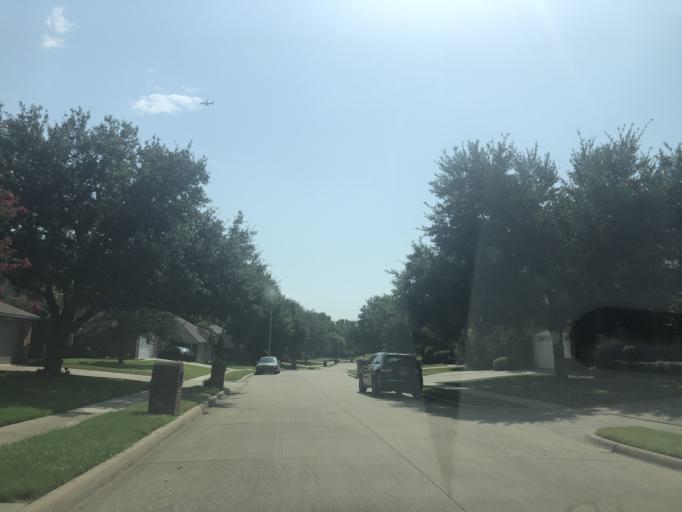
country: US
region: Texas
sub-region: Dallas County
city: Grand Prairie
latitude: 32.7706
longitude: -97.0407
